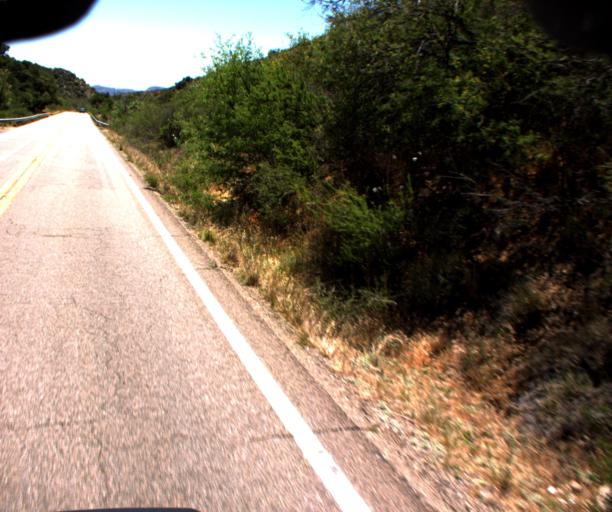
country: US
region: Arizona
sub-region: Gila County
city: Globe
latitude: 33.2228
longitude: -110.7906
